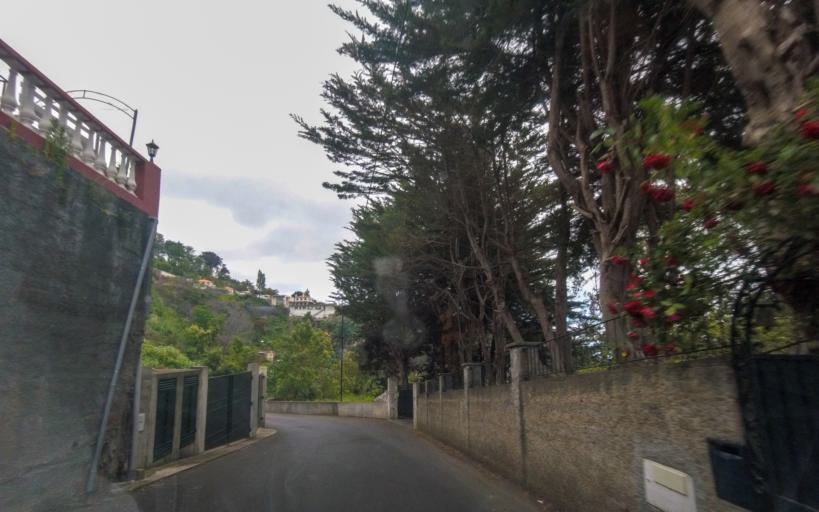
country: PT
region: Madeira
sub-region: Funchal
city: Nossa Senhora do Monte
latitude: 32.6763
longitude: -16.9131
